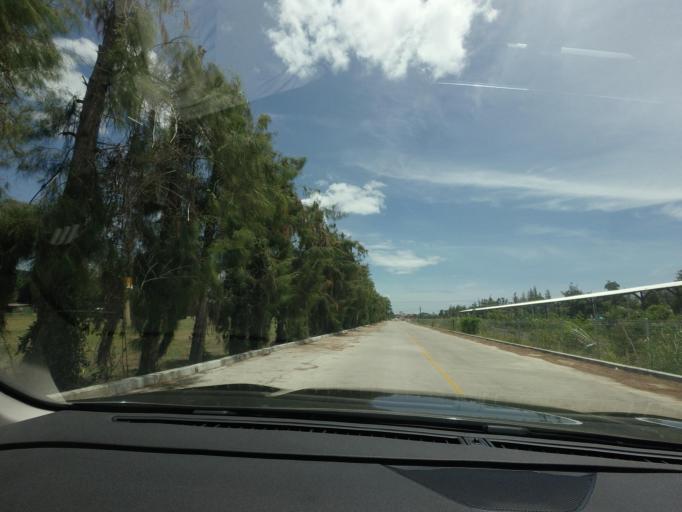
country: TH
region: Prachuap Khiri Khan
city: Hua Hin
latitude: 12.4964
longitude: 99.9722
